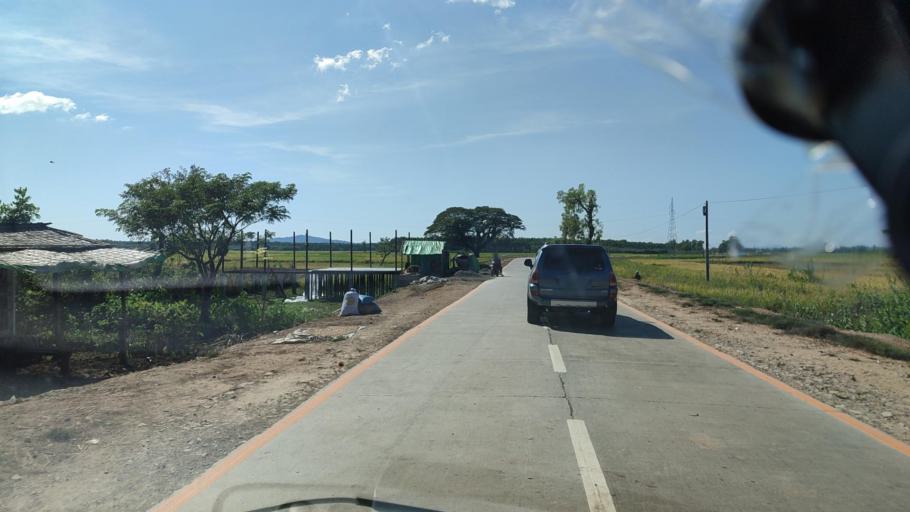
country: MM
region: Rakhine
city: Sittwe
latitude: 20.4781
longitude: 93.2852
